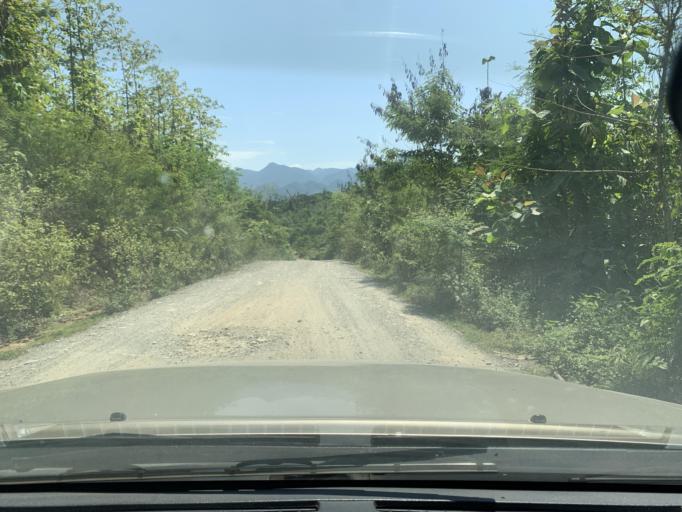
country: LA
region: Louangphabang
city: Louangphabang
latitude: 19.8981
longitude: 102.2137
